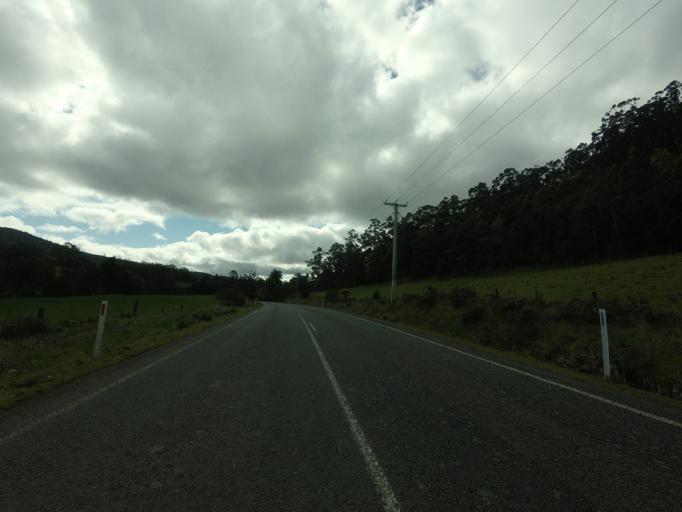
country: AU
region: Tasmania
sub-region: Huon Valley
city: Cygnet
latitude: -43.2810
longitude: 147.0105
